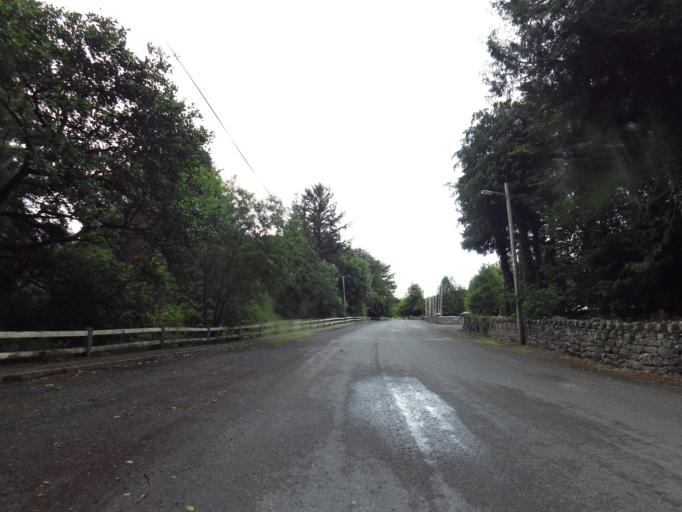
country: IE
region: Connaught
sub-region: County Galway
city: Athenry
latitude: 53.2831
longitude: -8.6811
